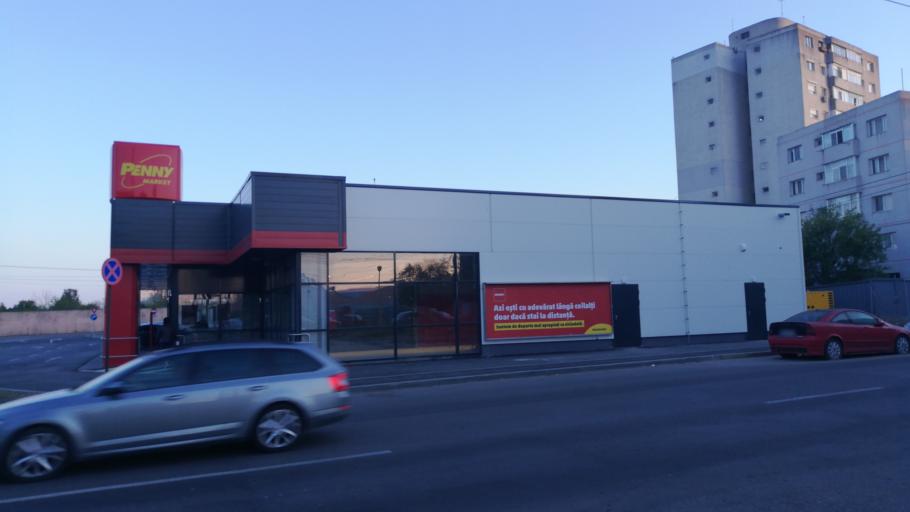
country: RO
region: Constanta
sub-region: Municipiul Constanta
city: Constanta
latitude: 44.1771
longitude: 28.6235
